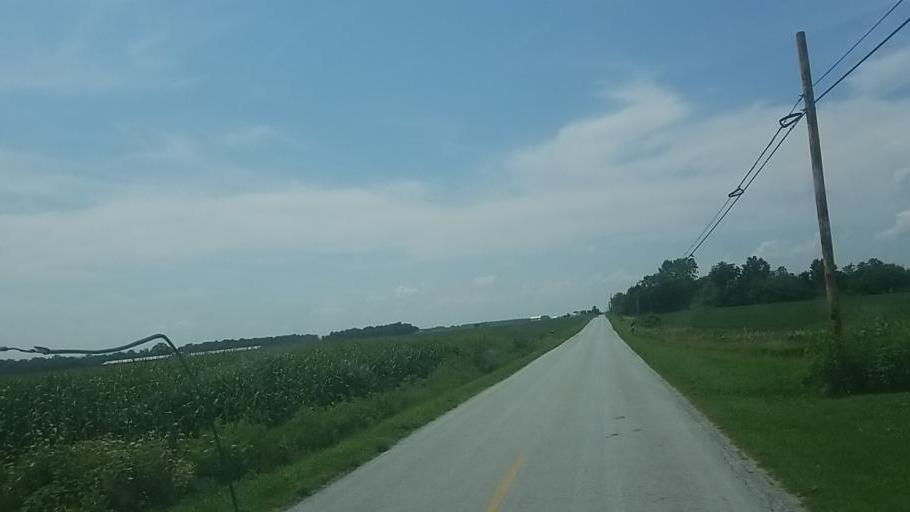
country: US
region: Ohio
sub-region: Hardin County
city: Kenton
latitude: 40.6575
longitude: -83.4885
